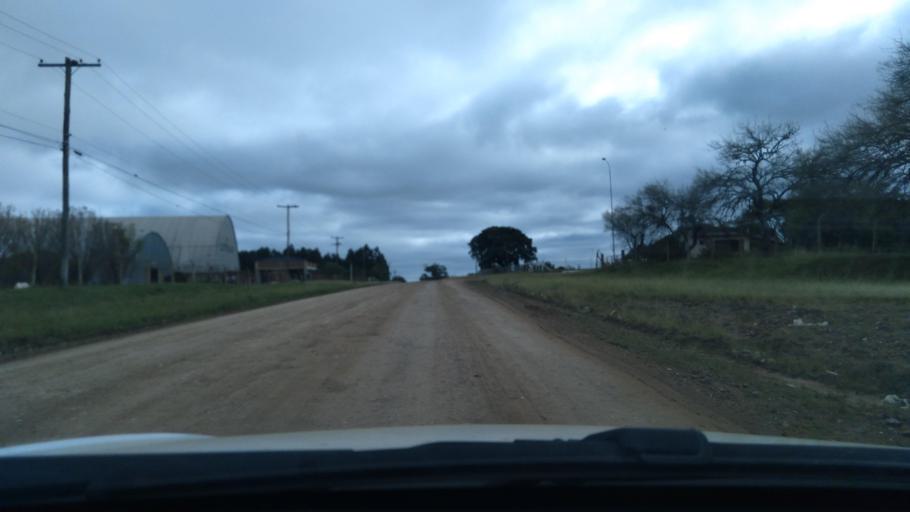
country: BR
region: Rio Grande do Sul
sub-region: Dom Pedrito
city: Dom Pedrito
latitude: -30.9829
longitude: -54.6430
